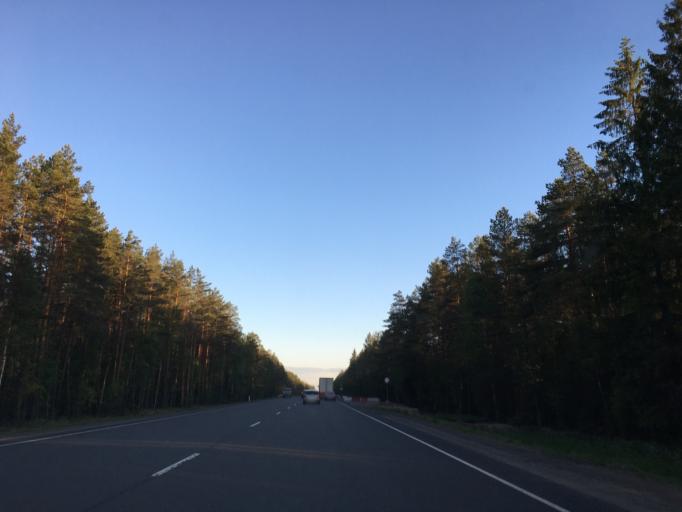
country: RU
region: Leningrad
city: Rozhdestveno
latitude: 59.2874
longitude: 29.9390
